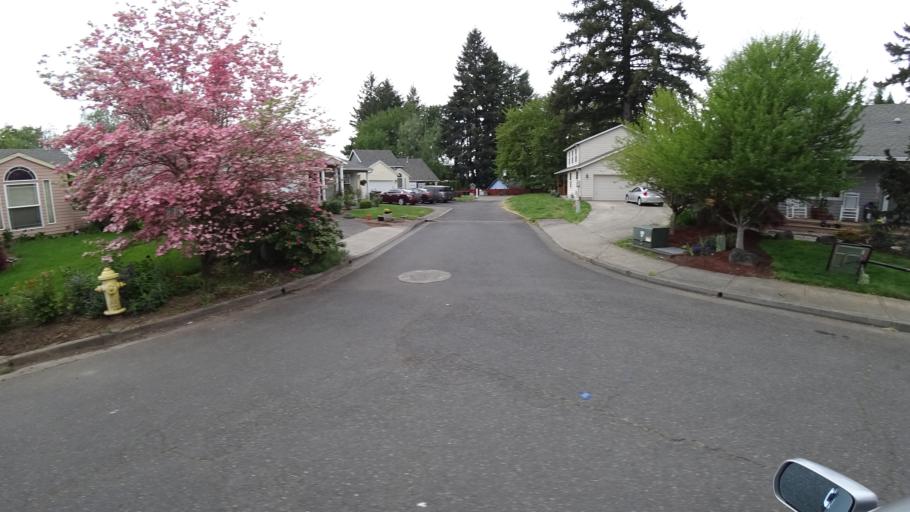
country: US
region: Oregon
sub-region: Washington County
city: Hillsboro
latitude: 45.5348
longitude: -122.9910
